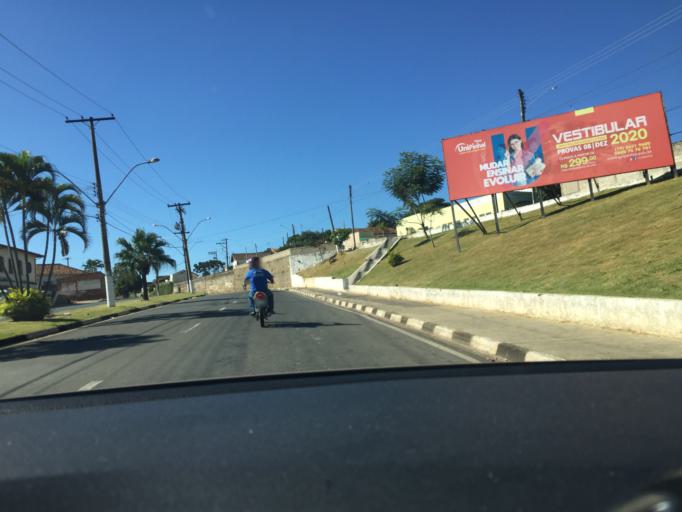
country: BR
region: Sao Paulo
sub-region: Santo Antonio Do Jardim
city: Espirito Santo do Pinhal
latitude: -22.1966
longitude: -46.7670
